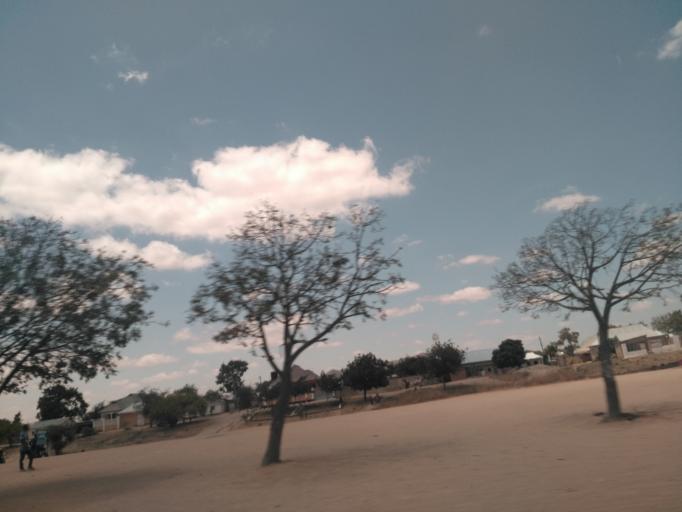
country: TZ
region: Dodoma
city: Kisasa
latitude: -6.1729
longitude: 35.7674
